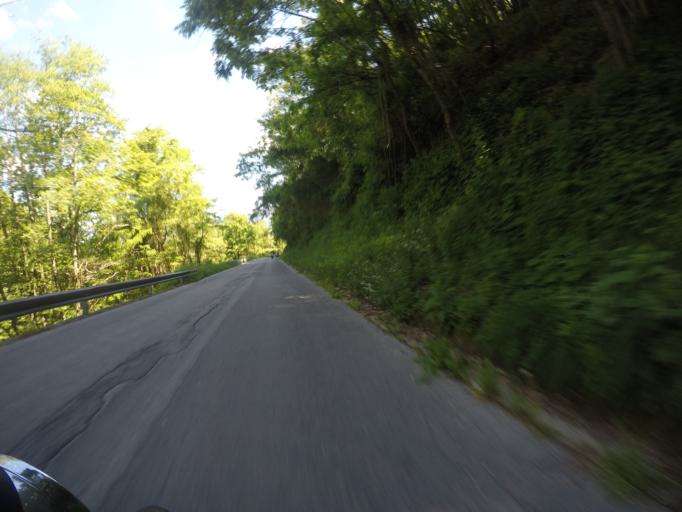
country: IT
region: Tuscany
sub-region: Provincia di Lucca
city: Careggine
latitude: 44.1239
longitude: 10.3324
